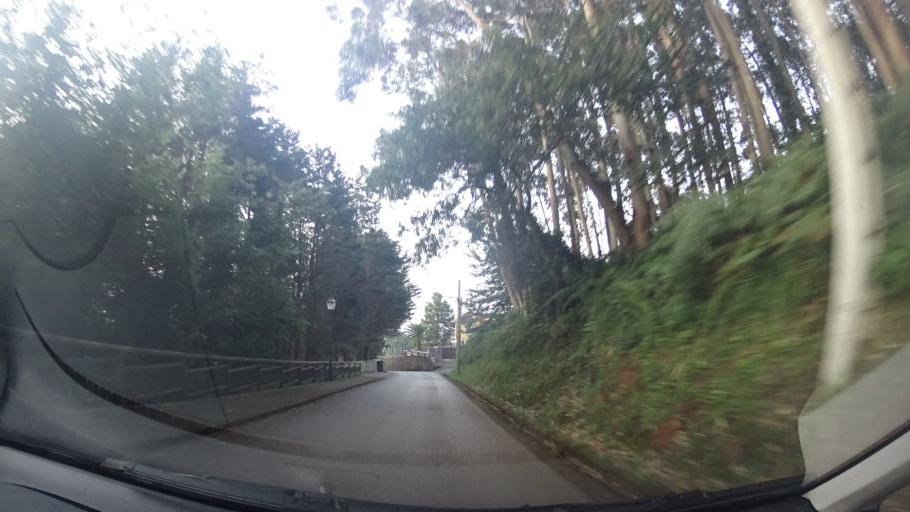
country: ES
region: Asturias
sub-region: Province of Asturias
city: Colunga
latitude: 43.4615
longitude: -5.2018
